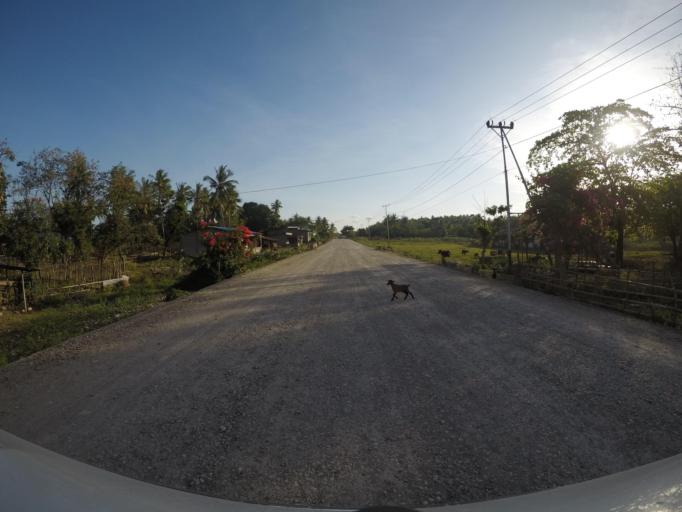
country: TL
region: Viqueque
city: Viqueque
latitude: -8.8054
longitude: 126.5455
